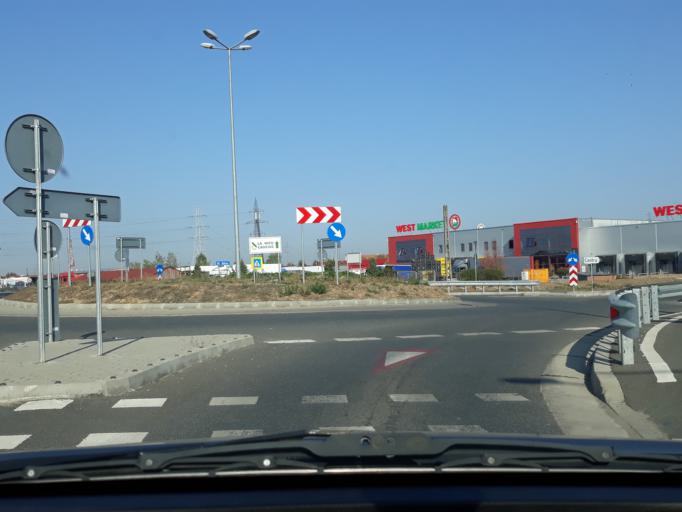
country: RO
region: Bihor
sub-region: Comuna Sanmartin
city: Sanmartin
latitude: 47.0293
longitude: 21.9444
